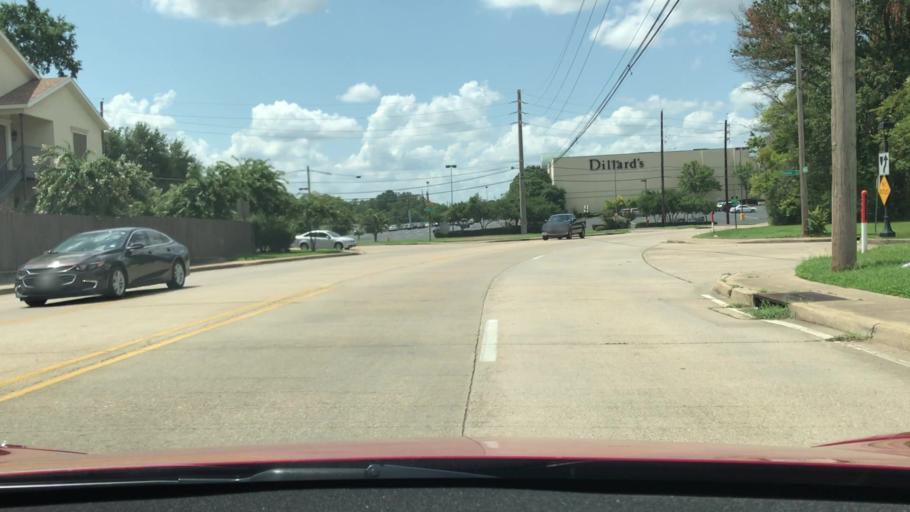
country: US
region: Louisiana
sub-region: Bossier Parish
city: Bossier City
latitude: 32.4810
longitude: -93.7522
